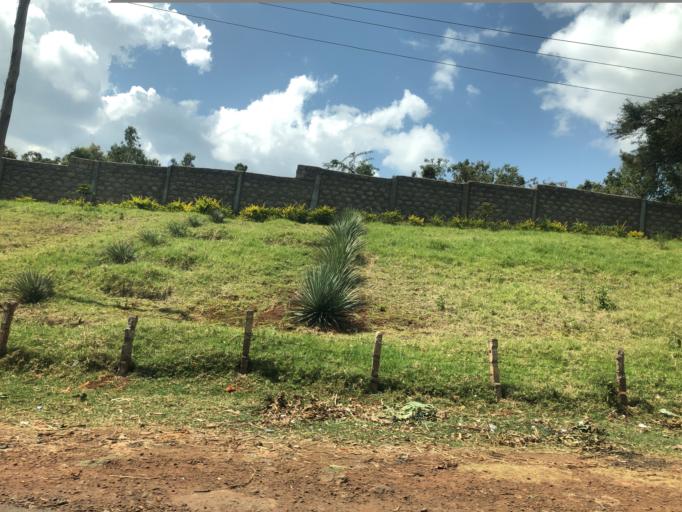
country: ET
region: Southern Nations, Nationalities, and People's Region
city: Boditi
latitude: 6.8693
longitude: 37.7669
